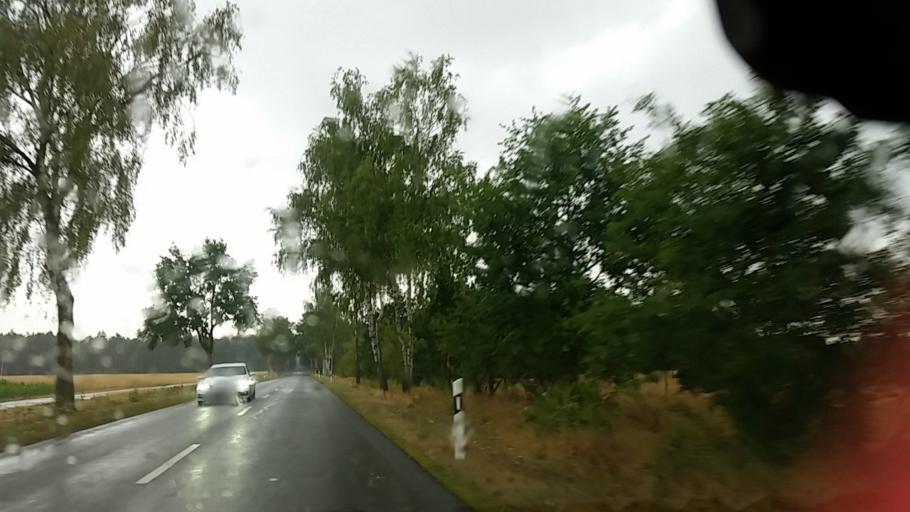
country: DE
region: Lower Saxony
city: Bokensdorf
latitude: 52.5372
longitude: 10.7176
